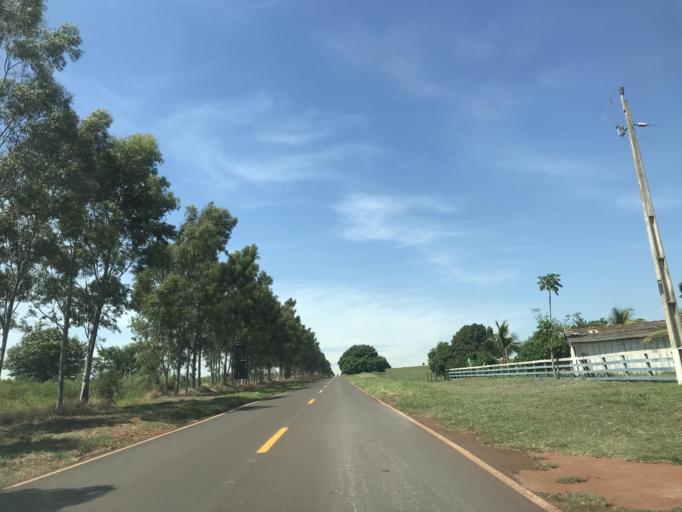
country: BR
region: Parana
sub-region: Paranavai
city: Nova Aurora
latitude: -22.8237
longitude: -52.6554
